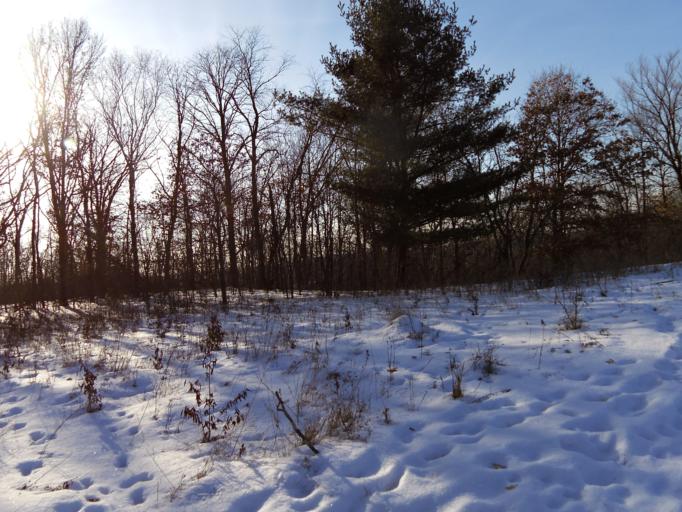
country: US
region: Wisconsin
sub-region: Saint Croix County
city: North Hudson
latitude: 45.0225
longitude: -92.6739
